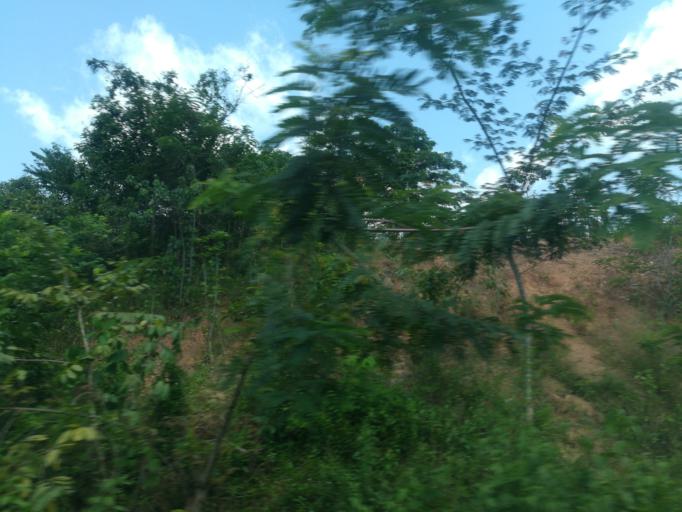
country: NG
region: Oyo
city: Moniya
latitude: 7.5845
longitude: 3.9137
